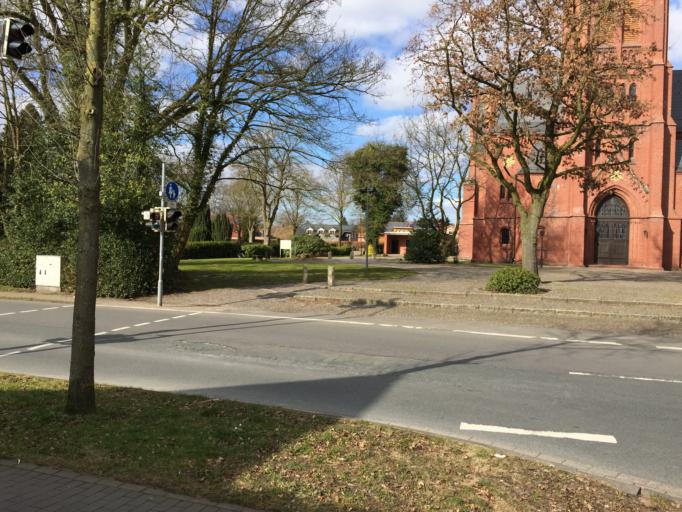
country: DE
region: Lower Saxony
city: Oldenburg
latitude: 53.1674
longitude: 8.2475
